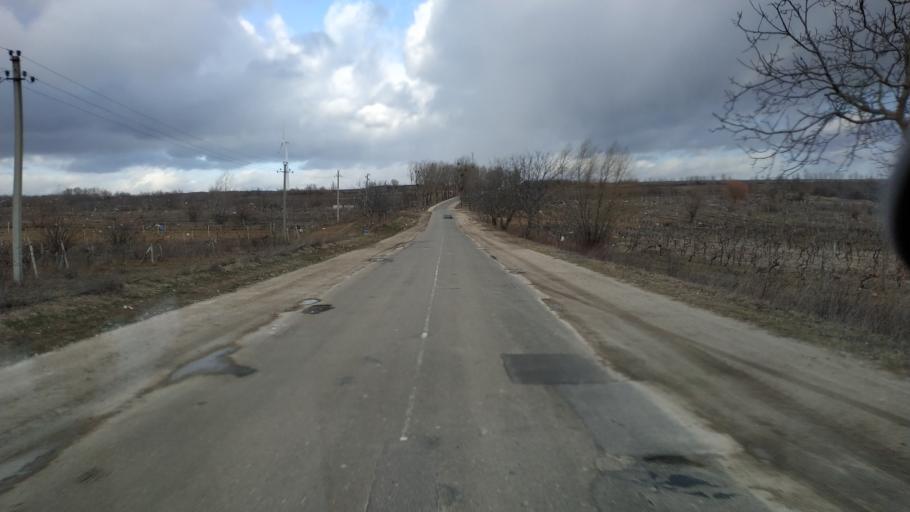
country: MD
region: Calarasi
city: Calarasi
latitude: 47.2823
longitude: 28.3313
